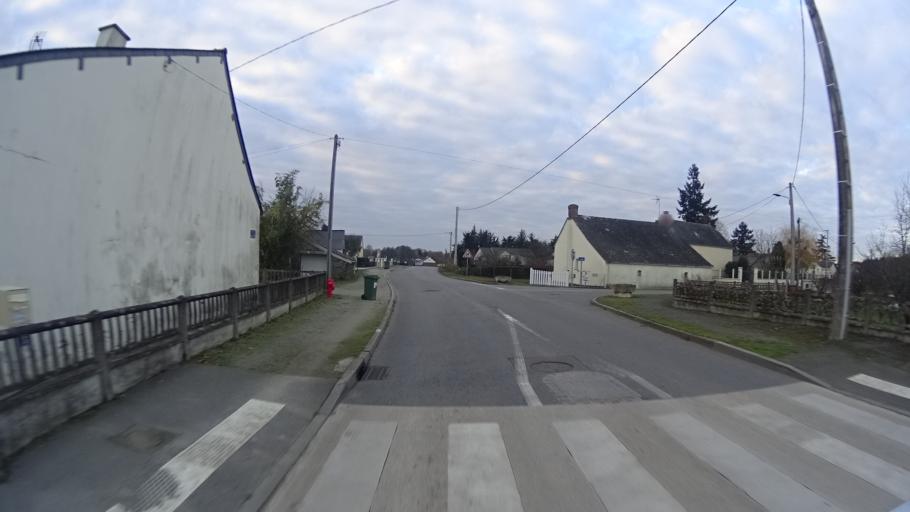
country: FR
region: Brittany
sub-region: Departement d'Ille-et-Vilaine
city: Langon
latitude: 47.6939
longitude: -1.8681
